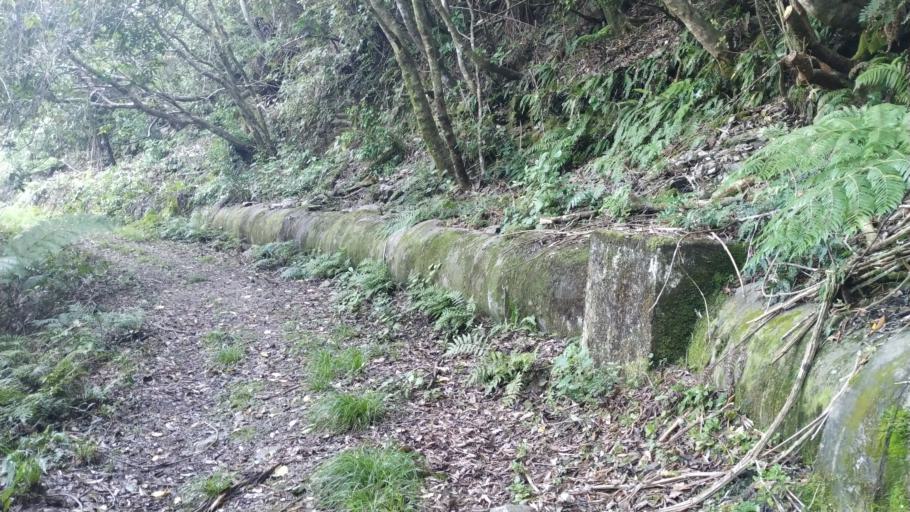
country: NZ
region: Nelson
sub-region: Nelson City
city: Nelson
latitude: -41.2928
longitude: 173.3351
